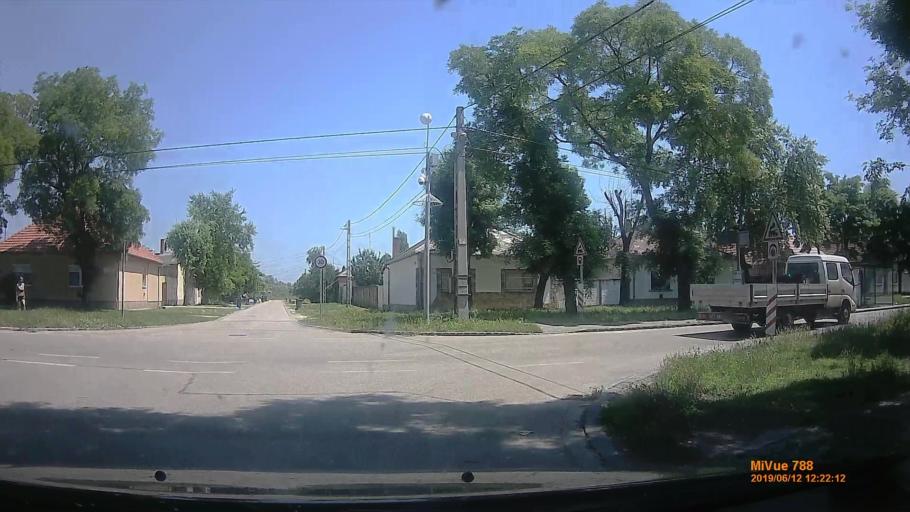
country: HU
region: Bacs-Kiskun
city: Kecskemet
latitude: 46.8979
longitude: 19.6977
